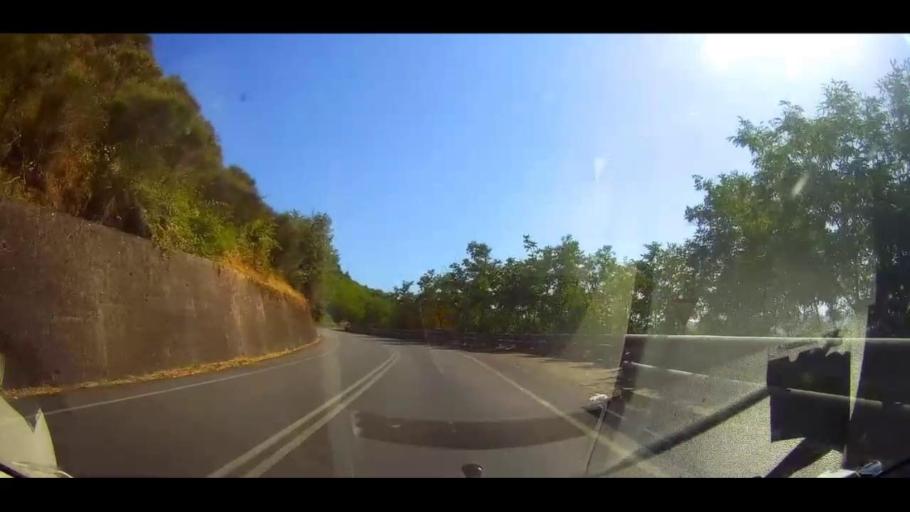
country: IT
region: Calabria
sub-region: Provincia di Cosenza
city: Cosenza
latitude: 39.3015
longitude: 16.2651
